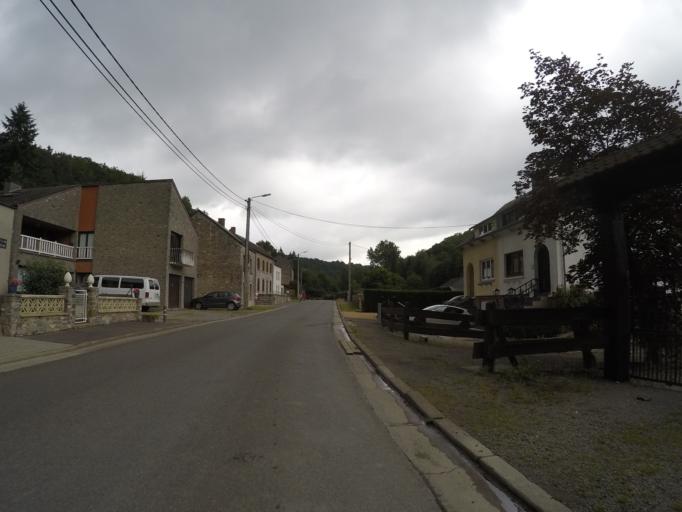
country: BE
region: Wallonia
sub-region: Province de Namur
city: Yvoir
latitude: 50.3324
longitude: 4.8968
